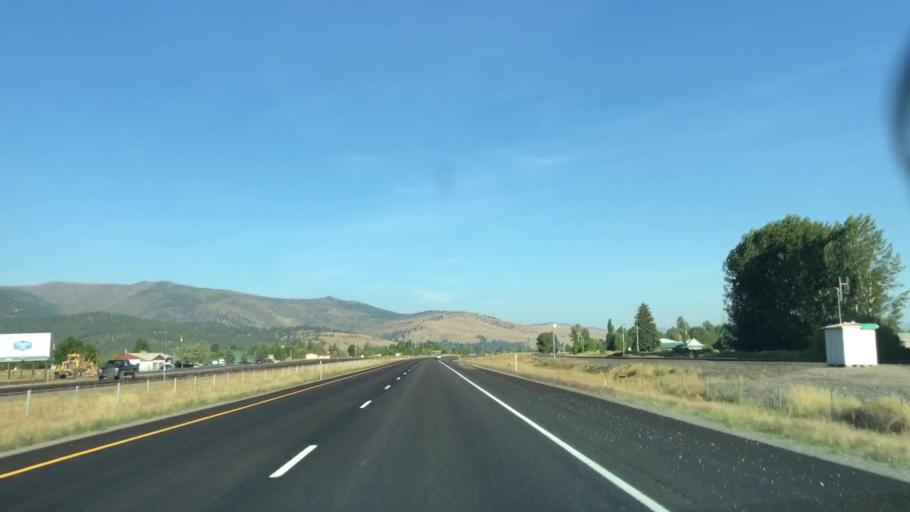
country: US
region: Montana
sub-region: Missoula County
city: Frenchtown
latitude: 47.0257
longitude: -114.2789
